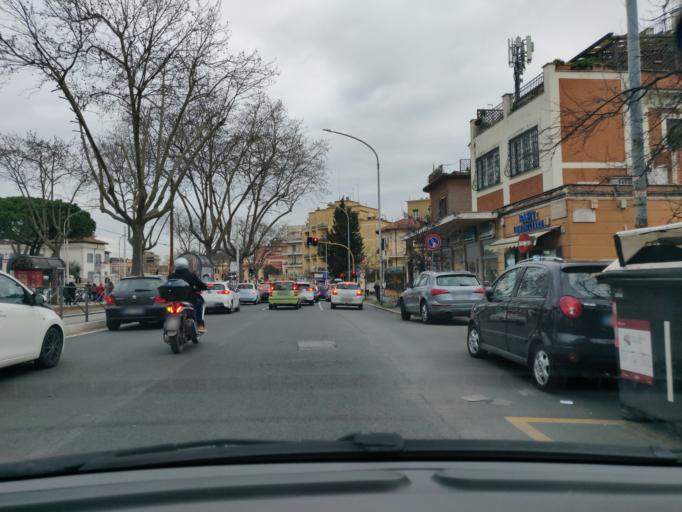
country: VA
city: Vatican City
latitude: 41.8718
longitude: 12.4496
